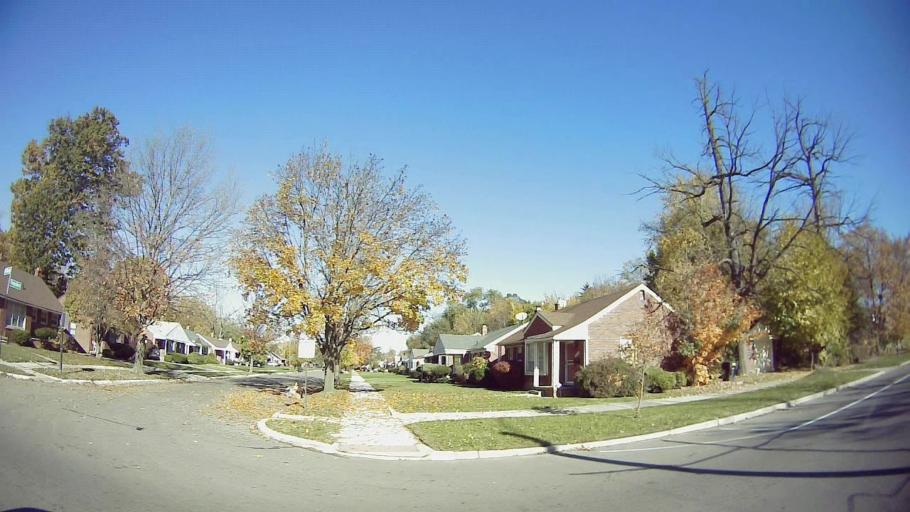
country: US
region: Michigan
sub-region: Wayne County
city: Dearborn Heights
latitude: 42.3647
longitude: -83.2390
